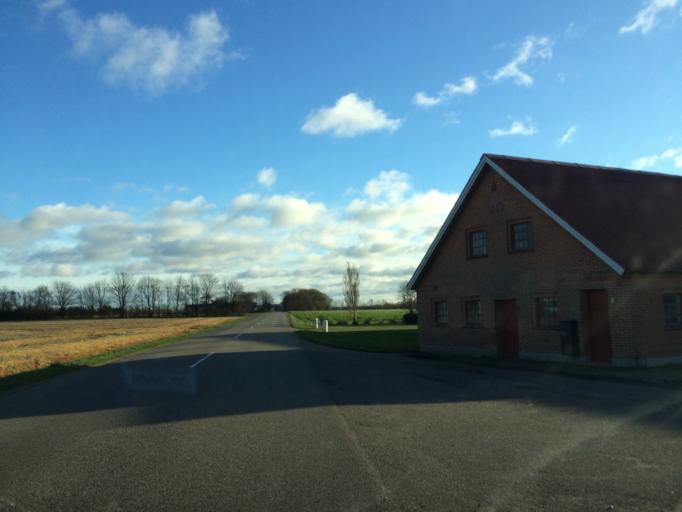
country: DK
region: Central Jutland
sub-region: Herning Kommune
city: Kibaek
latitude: 56.0048
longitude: 8.8602
